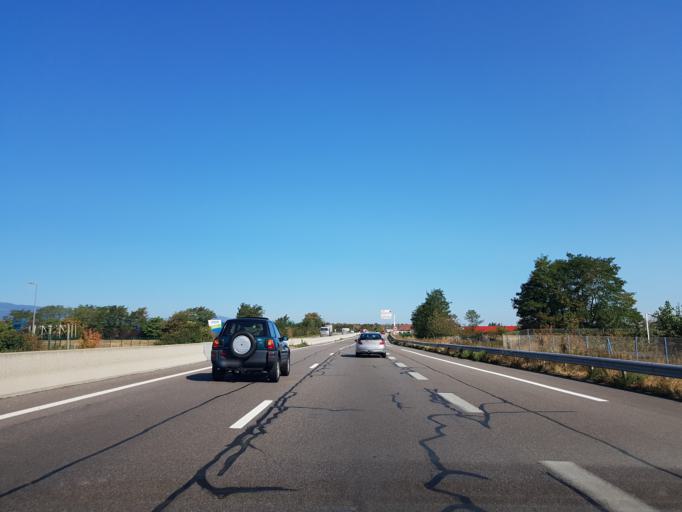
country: FR
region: Alsace
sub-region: Departement du Haut-Rhin
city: Kingersheim
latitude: 47.7935
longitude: 7.3116
